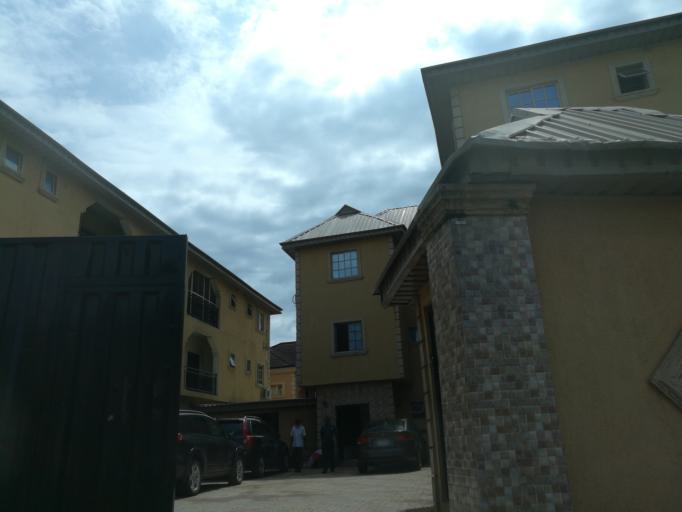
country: NG
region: Lagos
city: Agege
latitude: 6.6076
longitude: 3.3181
